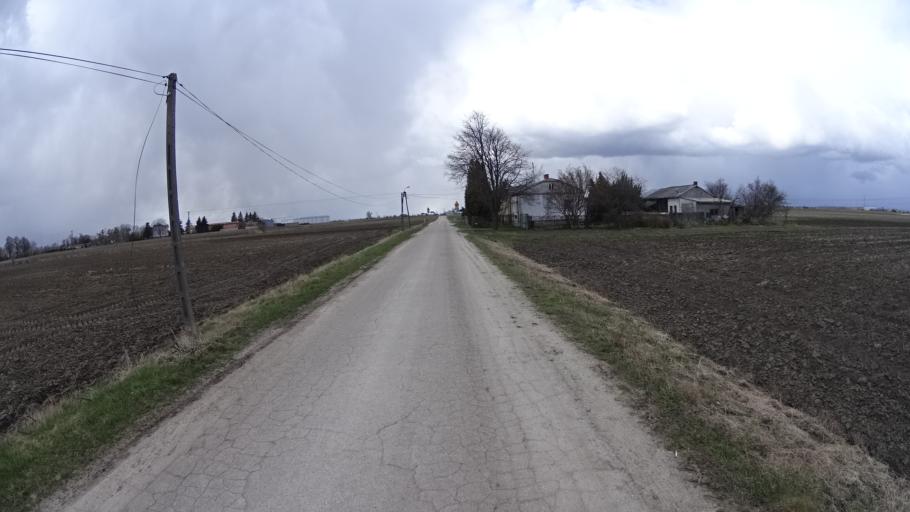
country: PL
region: Masovian Voivodeship
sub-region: Powiat warszawski zachodni
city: Jozefow
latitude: 52.2218
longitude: 20.6817
